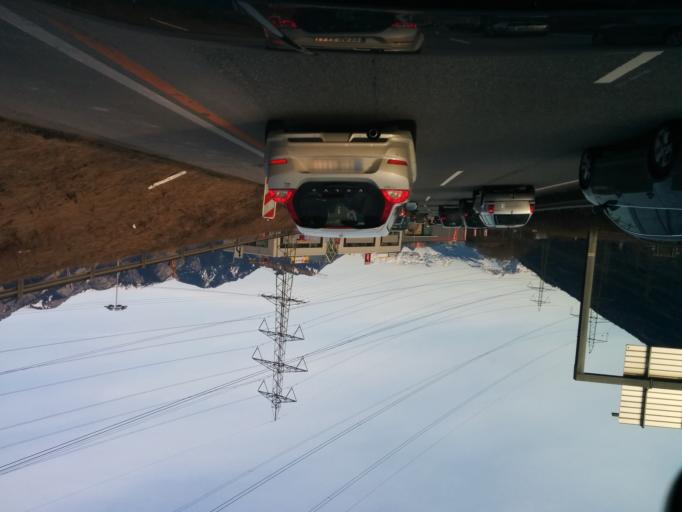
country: CH
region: Grisons
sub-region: Plessur District
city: Chur
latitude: 46.8478
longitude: 9.5049
